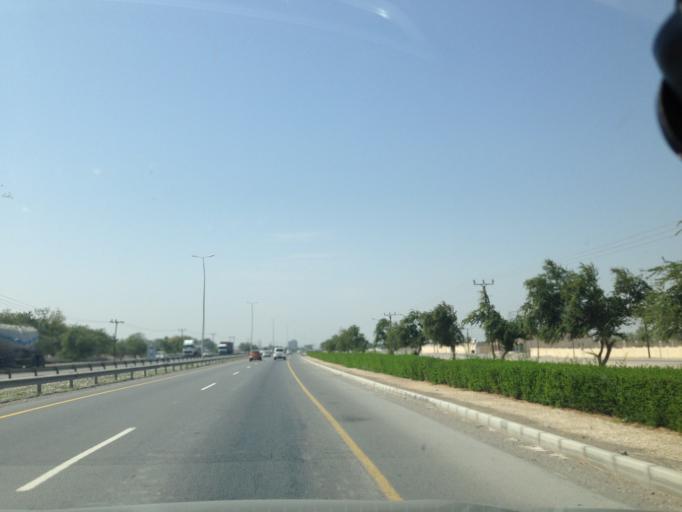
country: OM
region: Al Batinah
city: Barka'
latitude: 23.6594
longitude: 57.9239
